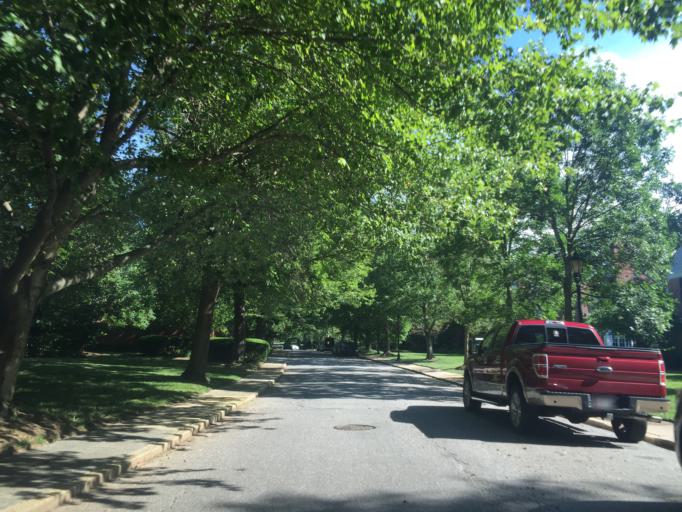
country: US
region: Maryland
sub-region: Baltimore County
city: Towson
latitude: 39.3615
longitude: -76.6200
